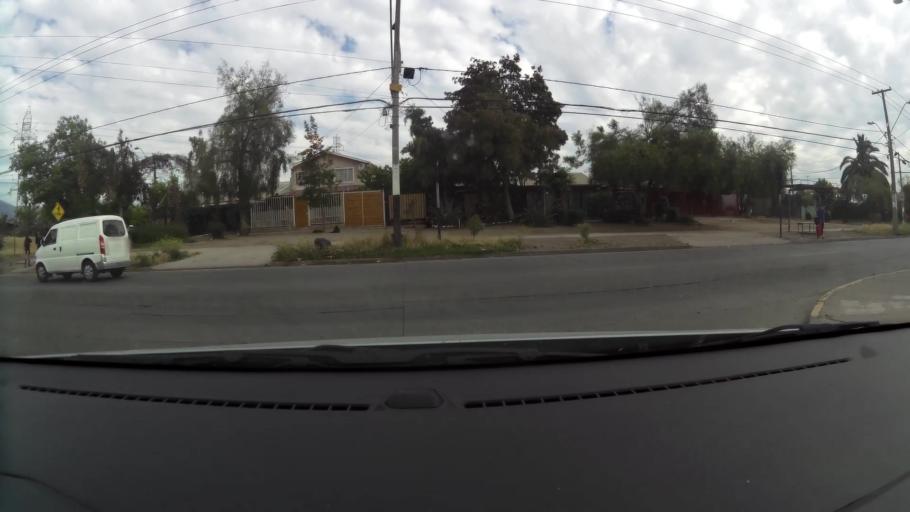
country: CL
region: Santiago Metropolitan
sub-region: Provincia de Santiago
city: La Pintana
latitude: -33.6174
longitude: -70.6184
